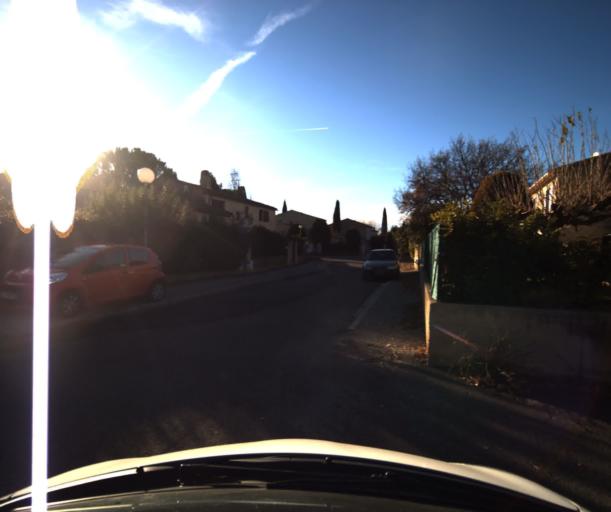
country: FR
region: Provence-Alpes-Cote d'Azur
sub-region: Departement du Vaucluse
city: Pertuis
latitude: 43.7078
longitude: 5.4943
